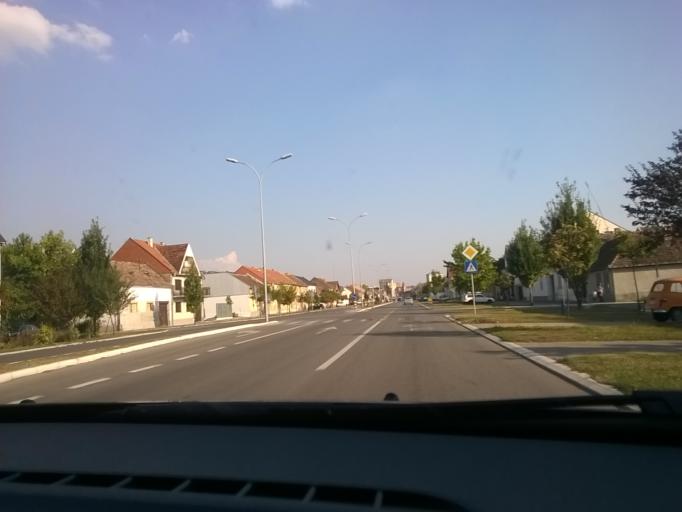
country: RS
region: Autonomna Pokrajina Vojvodina
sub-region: Juznobanatski Okrug
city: Vrsac
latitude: 45.1267
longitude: 21.2900
